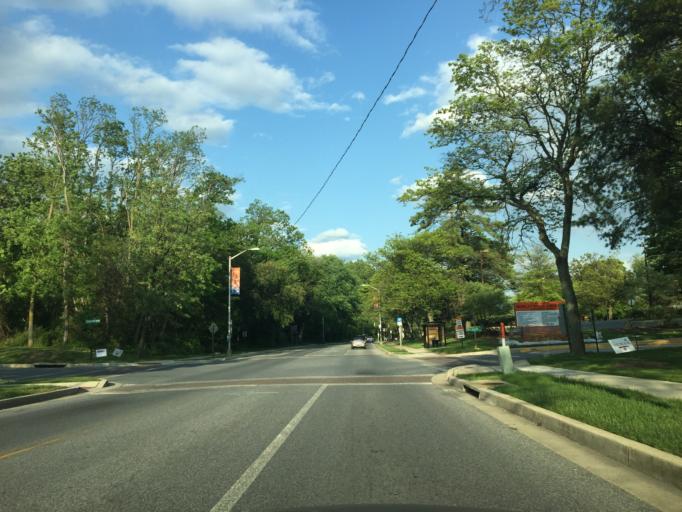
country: US
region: Maryland
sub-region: Baltimore County
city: Parkville
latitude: 39.3404
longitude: -76.5826
